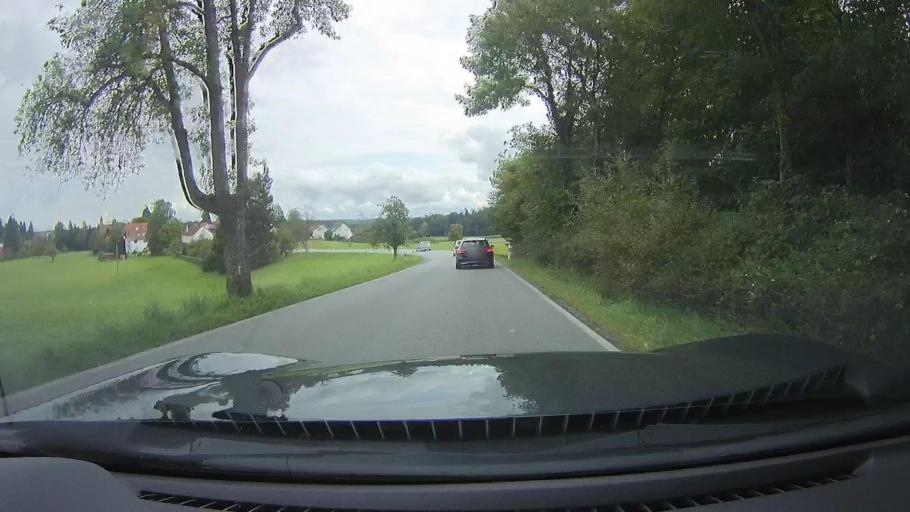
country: DE
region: Baden-Wuerttemberg
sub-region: Regierungsbezirk Stuttgart
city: Mainhardt
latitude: 49.0360
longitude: 9.5732
